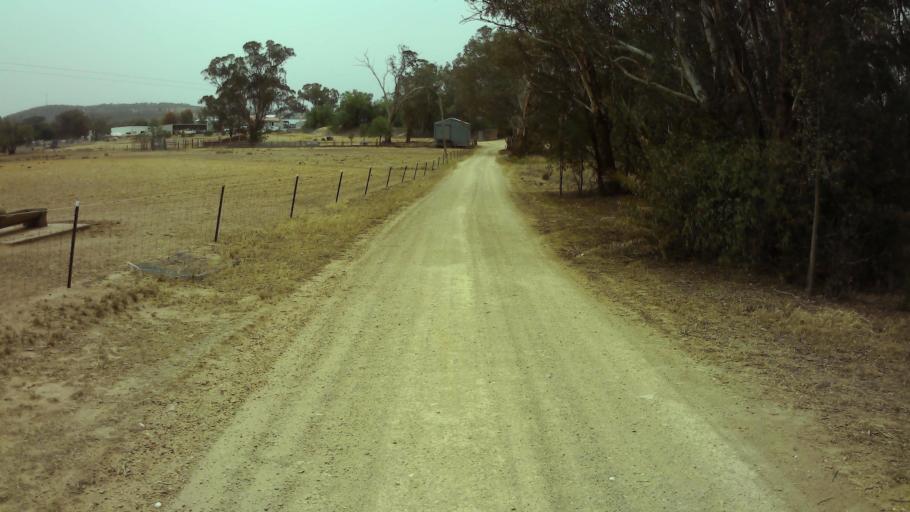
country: AU
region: New South Wales
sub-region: Weddin
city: Grenfell
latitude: -33.9050
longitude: 148.1542
